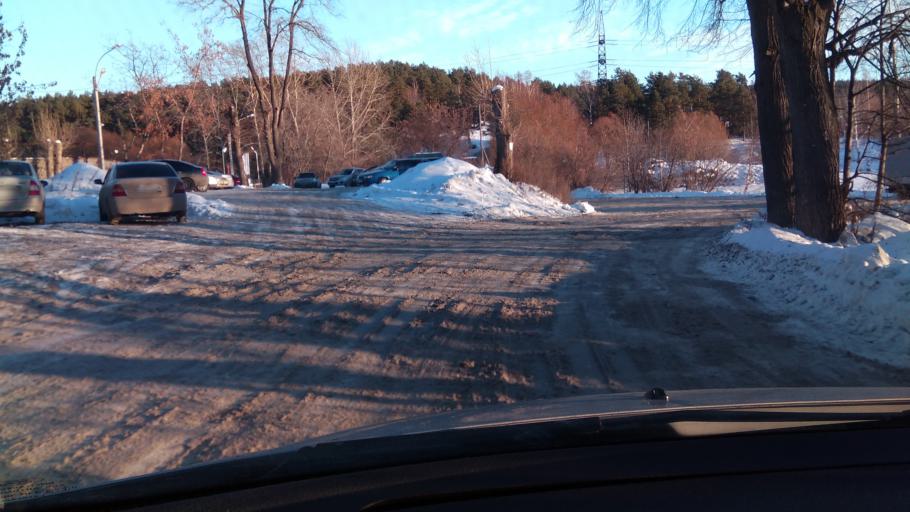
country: RU
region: Sverdlovsk
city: Sovkhoznyy
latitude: 56.7553
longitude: 60.6314
